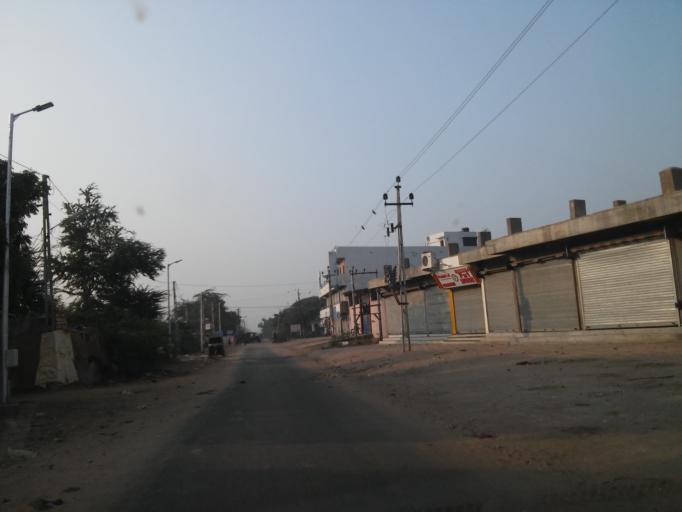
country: IN
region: Gujarat
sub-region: Kachchh
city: Mandvi
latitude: 22.8344
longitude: 69.3653
